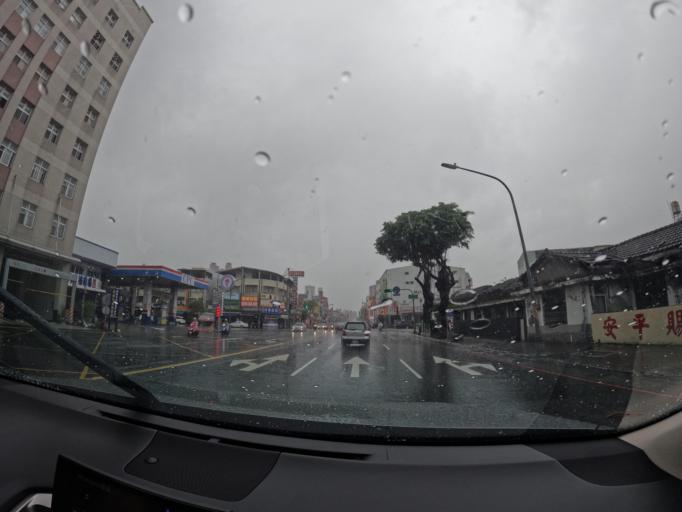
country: TW
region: Kaohsiung
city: Kaohsiung
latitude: 22.6672
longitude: 120.3219
